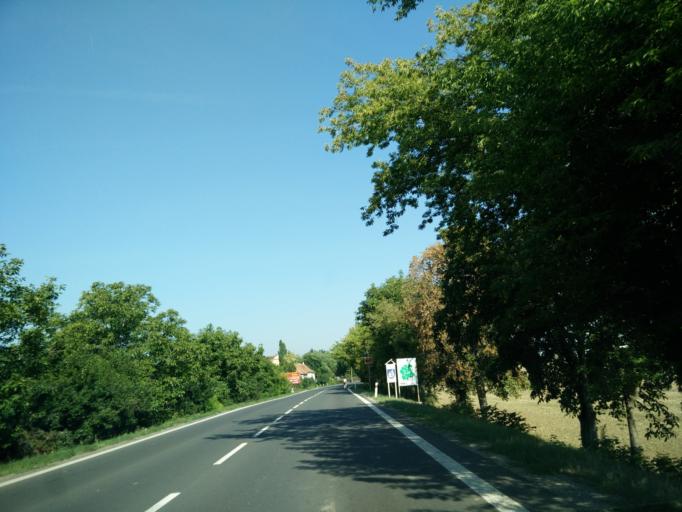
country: SK
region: Nitriansky
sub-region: Okres Nitra
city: Nitra
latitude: 48.3696
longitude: 18.0426
